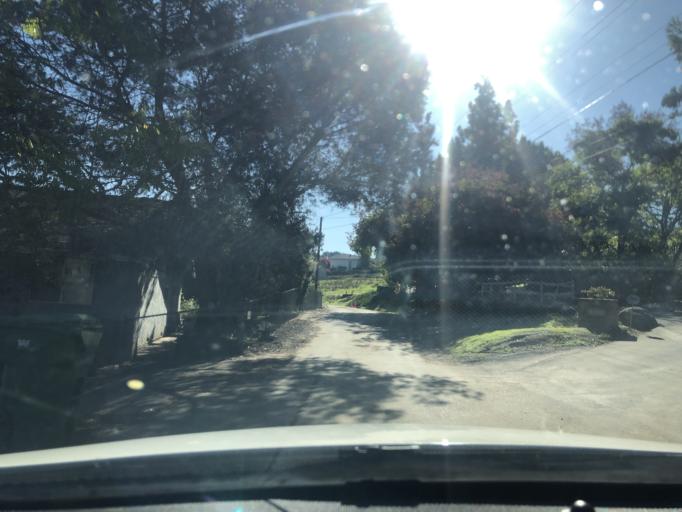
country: US
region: California
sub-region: San Diego County
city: Casa de Oro-Mount Helix
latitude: 32.7747
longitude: -116.9444
